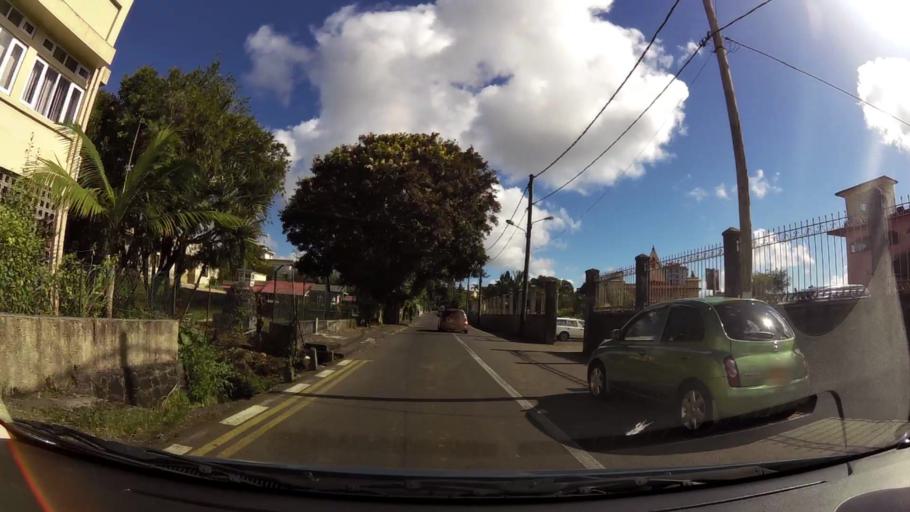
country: MU
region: Plaines Wilhems
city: Curepipe
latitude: -20.3226
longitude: 57.5291
